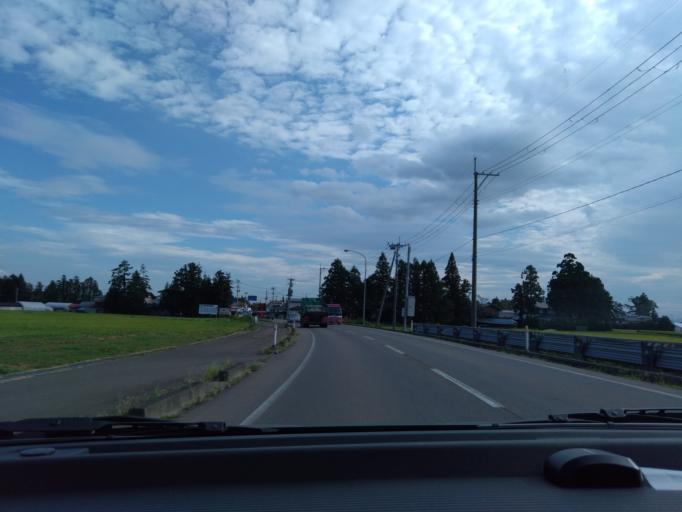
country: JP
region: Iwate
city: Hanamaki
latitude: 39.4469
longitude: 141.0977
